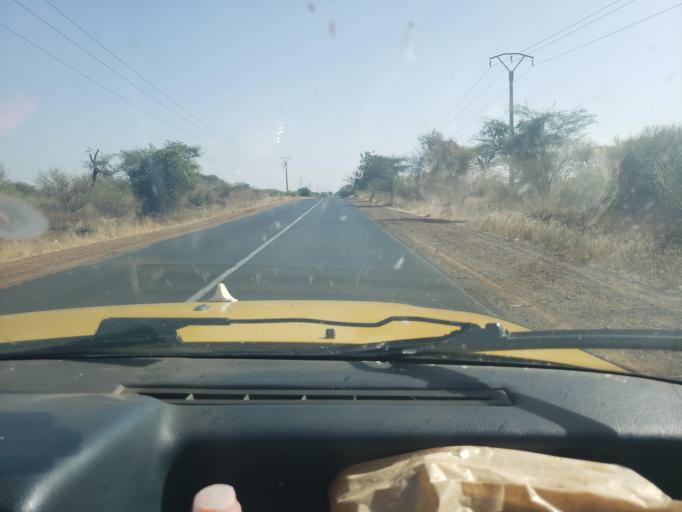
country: SN
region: Louga
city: Louga
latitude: 15.6625
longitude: -16.2583
